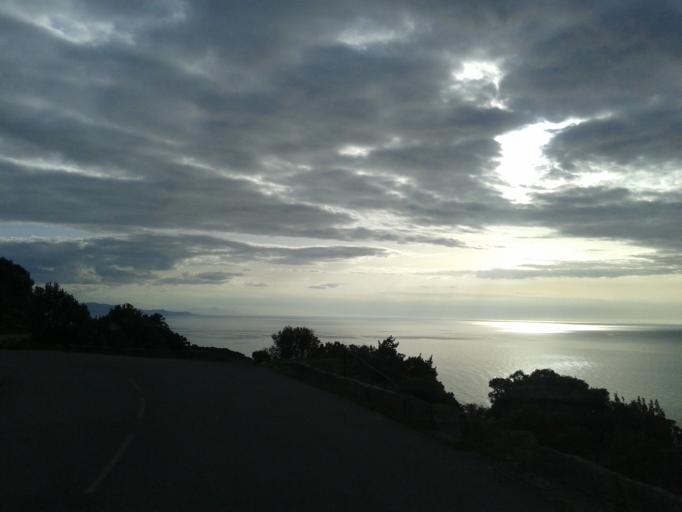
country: FR
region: Corsica
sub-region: Departement de la Haute-Corse
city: Brando
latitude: 42.8861
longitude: 9.3344
